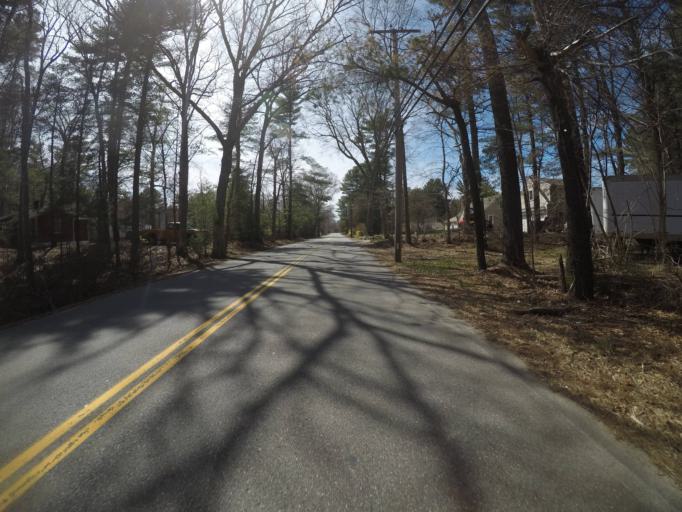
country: US
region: Massachusetts
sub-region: Bristol County
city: Easton
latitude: 42.0243
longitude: -71.0724
